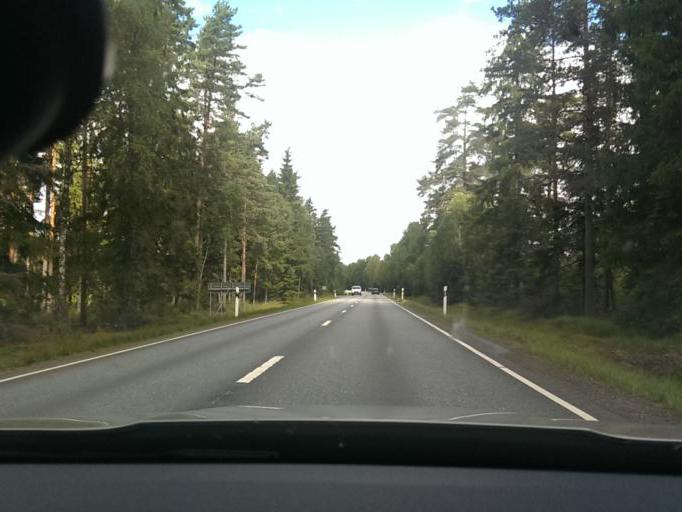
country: SE
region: Joenkoeping
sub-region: Varnamo Kommun
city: Varnamo
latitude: 57.2533
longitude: 13.9862
